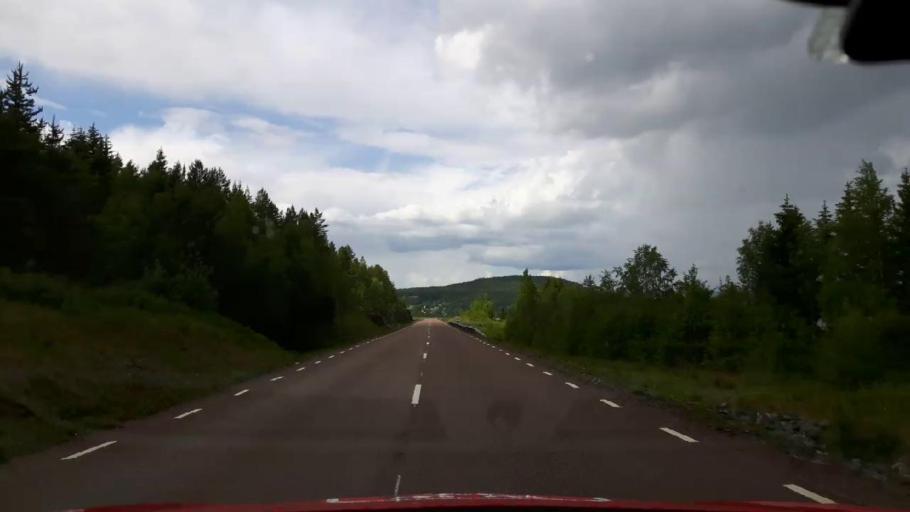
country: SE
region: Jaemtland
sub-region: Krokoms Kommun
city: Valla
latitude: 63.8966
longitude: 14.2526
